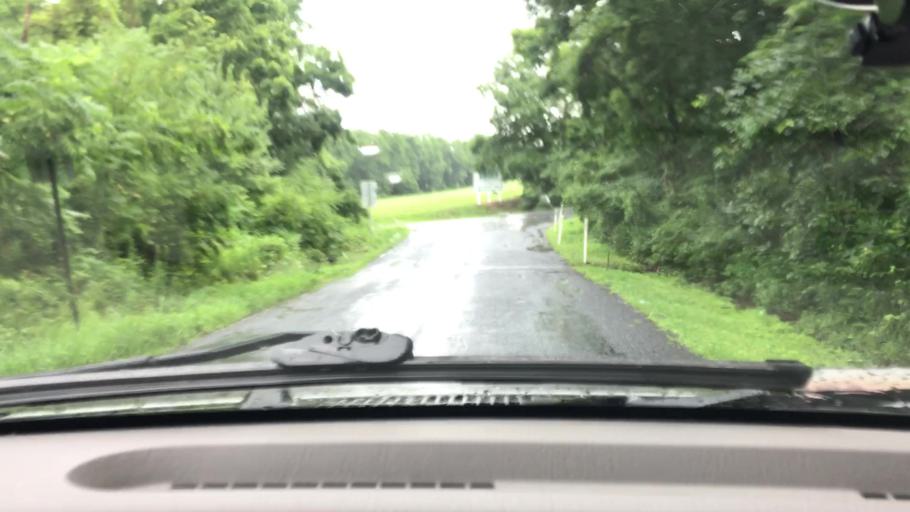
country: US
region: Pennsylvania
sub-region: Lancaster County
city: Elizabethtown
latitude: 40.1878
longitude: -76.5901
